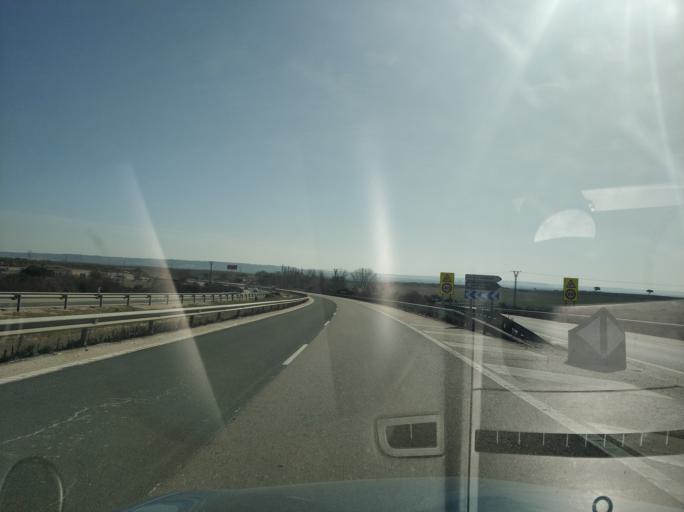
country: ES
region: Castille and Leon
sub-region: Provincia de Valladolid
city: Cisterniga
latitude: 41.6016
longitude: -4.6615
